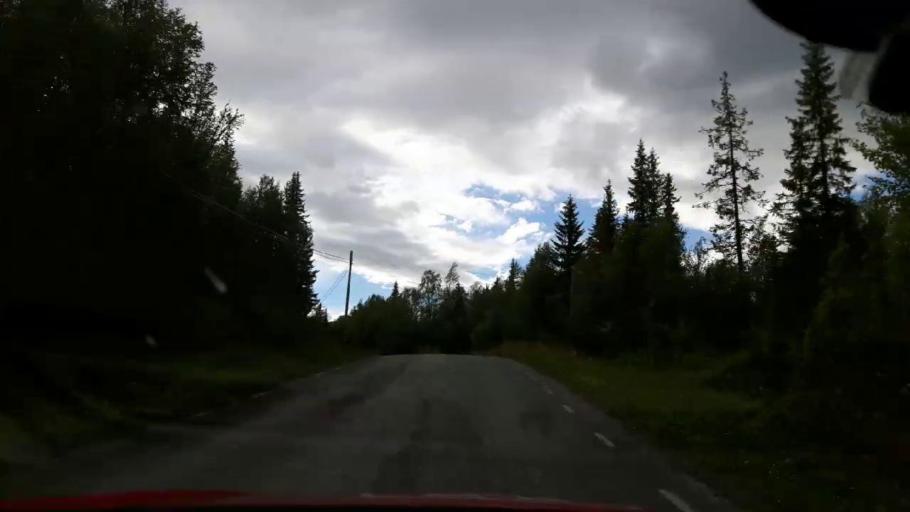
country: SE
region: Jaemtland
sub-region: Are Kommun
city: Are
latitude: 63.1566
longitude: 13.0317
